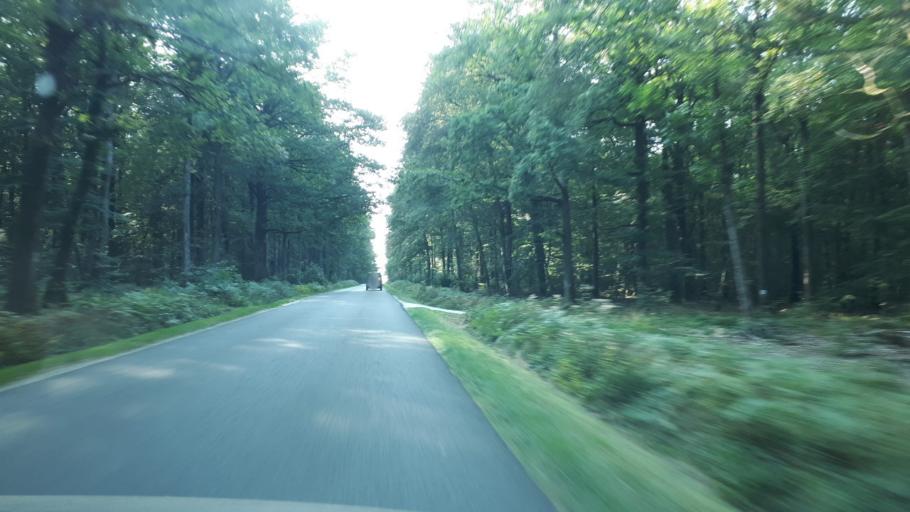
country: FR
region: Centre
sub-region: Departement du Cher
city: Saint-Eloy-de-Gy
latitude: 47.2184
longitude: 2.3568
